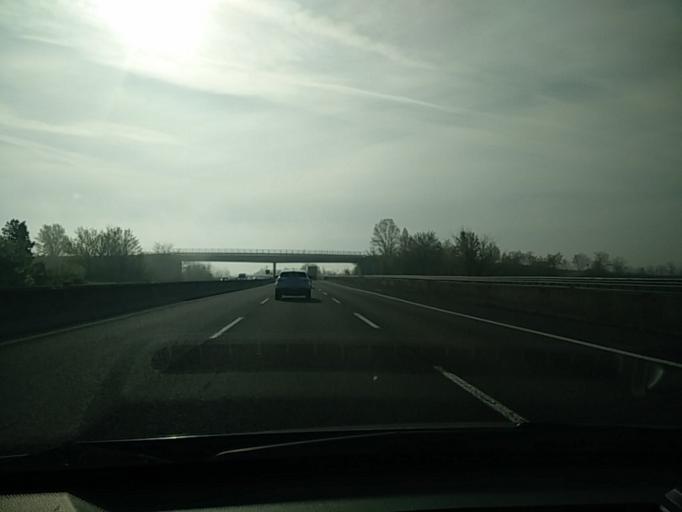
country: IT
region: Emilia-Romagna
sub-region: Provincia di Bologna
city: Ozzano dell'Emilia
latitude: 44.4673
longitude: 11.4827
